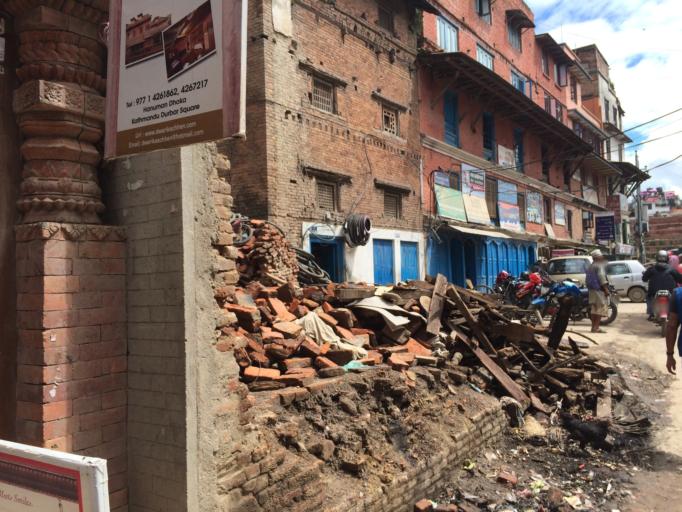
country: NP
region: Central Region
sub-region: Bagmati Zone
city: Kathmandu
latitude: 27.7050
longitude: 85.3063
